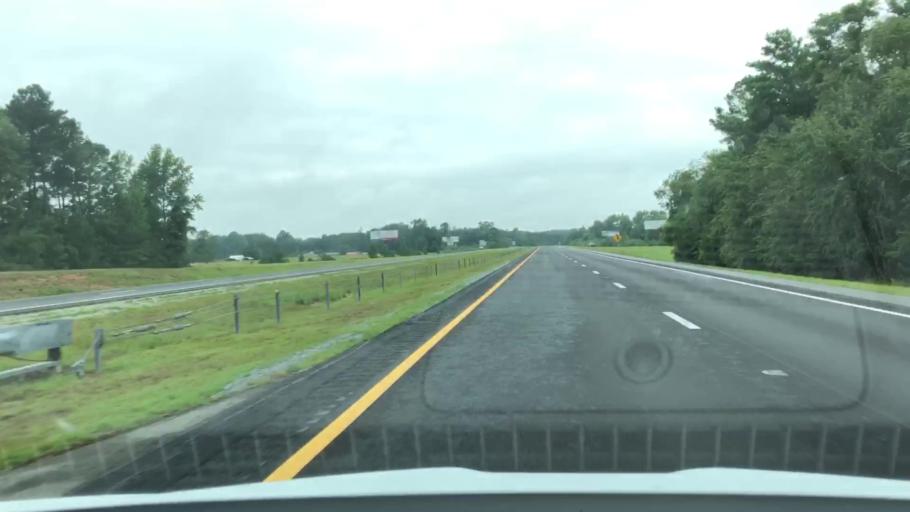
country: US
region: North Carolina
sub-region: Wayne County
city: Fremont
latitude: 35.4955
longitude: -77.9963
